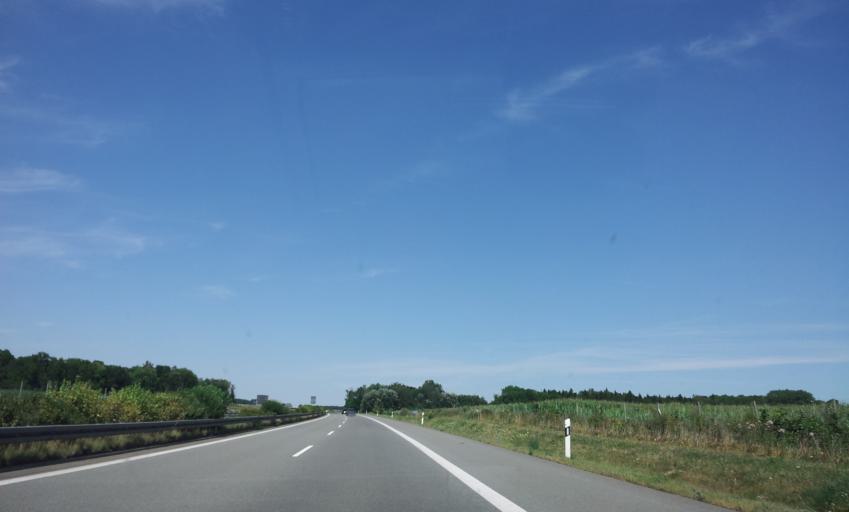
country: DE
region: Mecklenburg-Vorpommern
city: Jarmen
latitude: 53.9540
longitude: 13.3690
